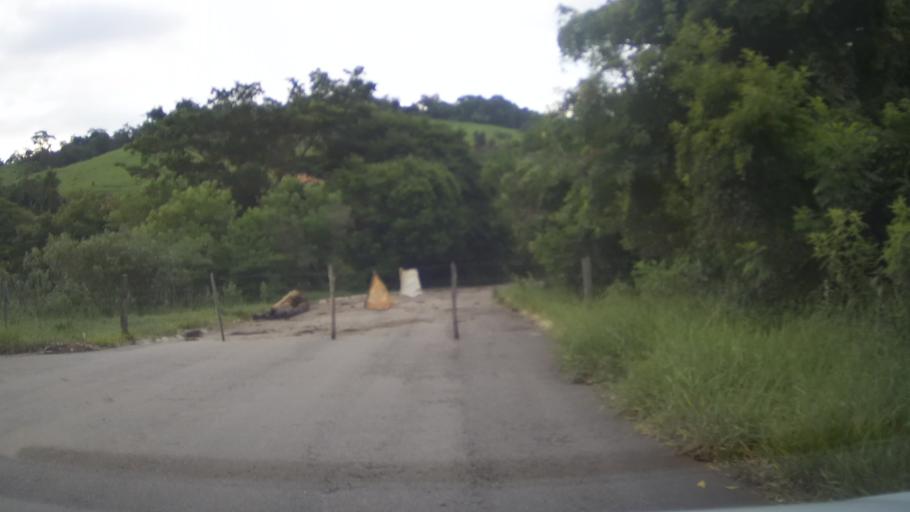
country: BR
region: Sao Paulo
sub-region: Vinhedo
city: Vinhedo
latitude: -23.0791
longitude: -47.0324
